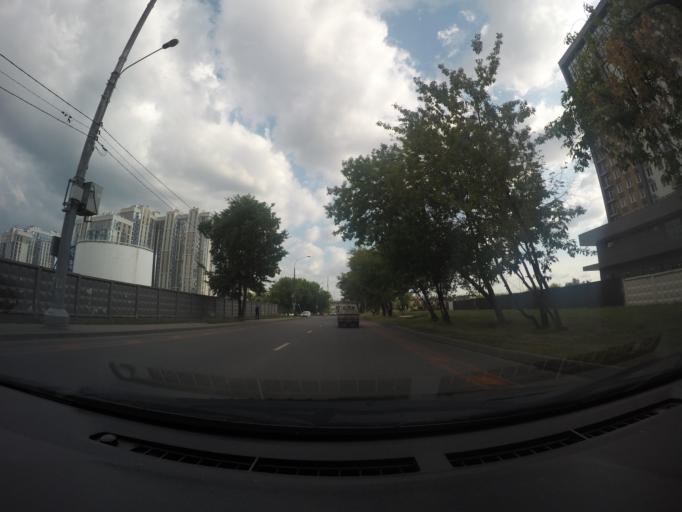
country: RU
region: Moscow
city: Sviblovo
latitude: 55.8495
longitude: 37.6262
